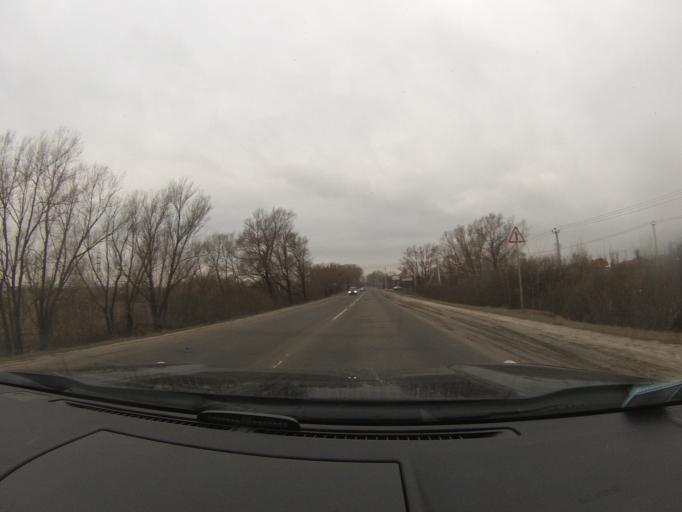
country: RU
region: Moskovskaya
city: Lopatinskiy
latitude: 55.3282
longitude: 38.7240
